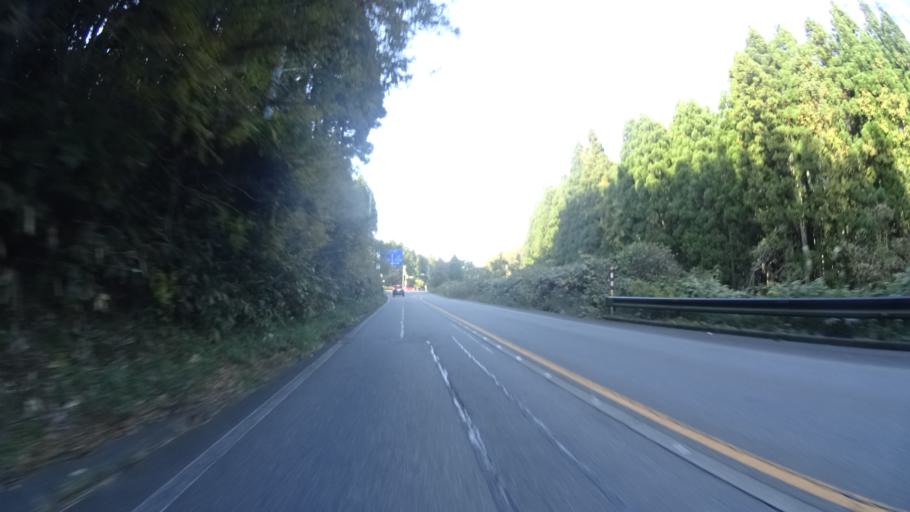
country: JP
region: Ishikawa
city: Hakui
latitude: 37.0618
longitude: 136.7795
